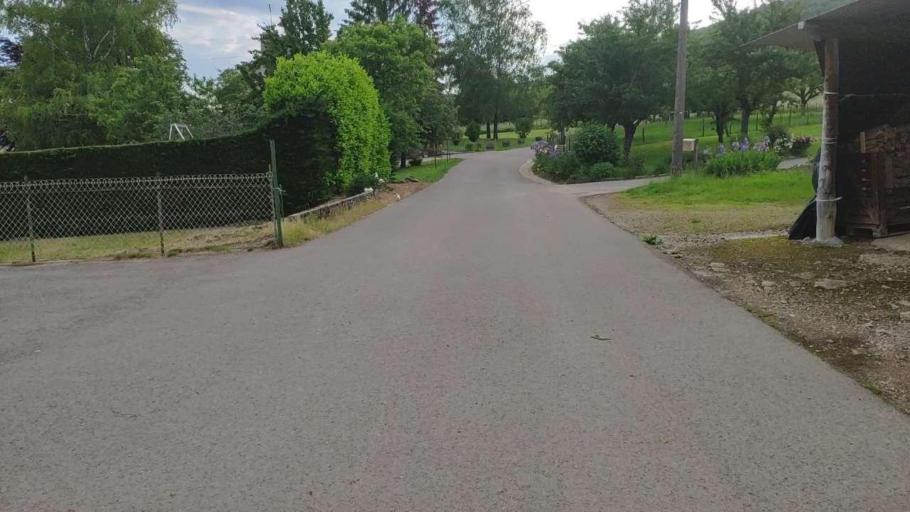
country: FR
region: Franche-Comte
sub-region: Departement du Jura
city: Perrigny
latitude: 46.7189
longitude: 5.5972
